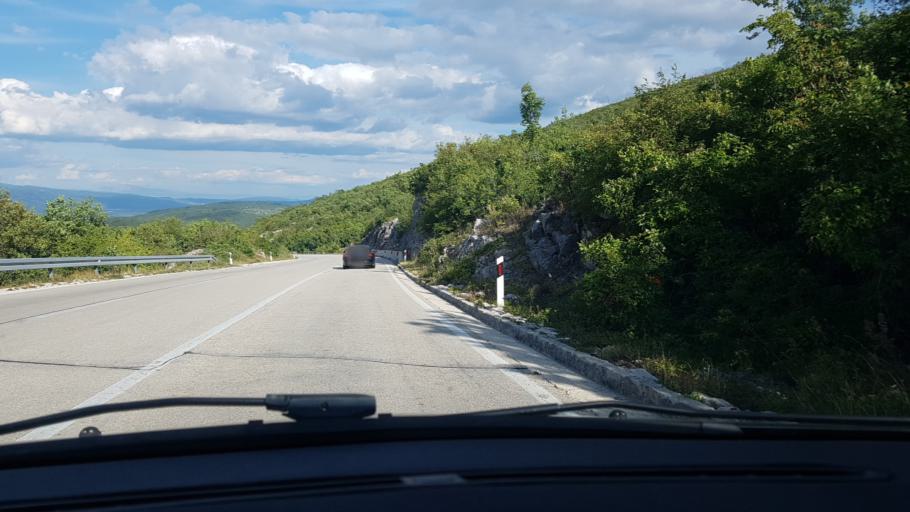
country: HR
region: Splitsko-Dalmatinska
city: Grubine
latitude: 43.4174
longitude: 17.1029
